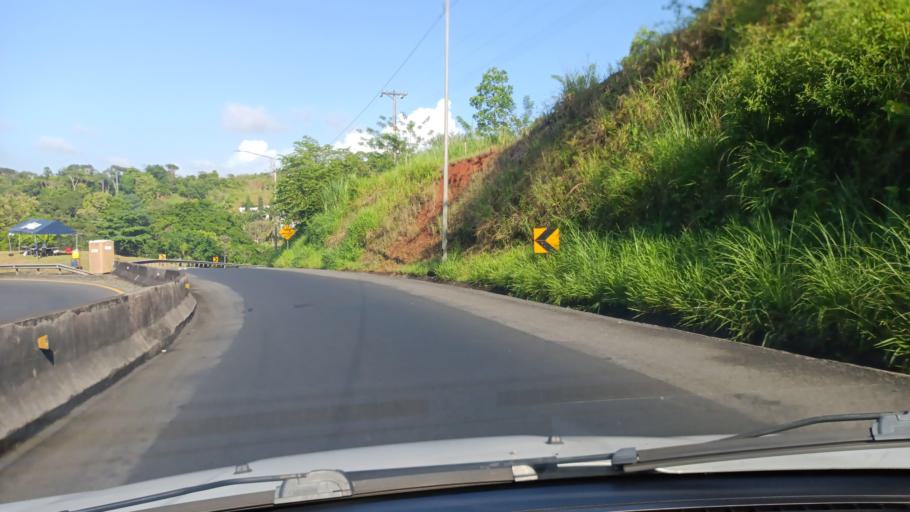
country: PA
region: Colon
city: Santa Rita Arriba
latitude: 9.3226
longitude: -79.7988
